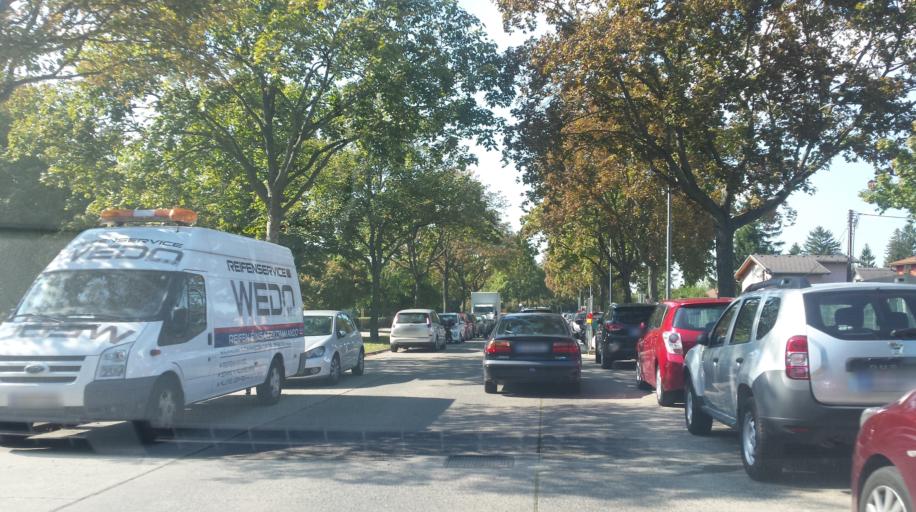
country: AT
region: Lower Austria
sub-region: Politischer Bezirk Wien-Umgebung
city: Leopoldsdorf
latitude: 48.1503
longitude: 16.3910
